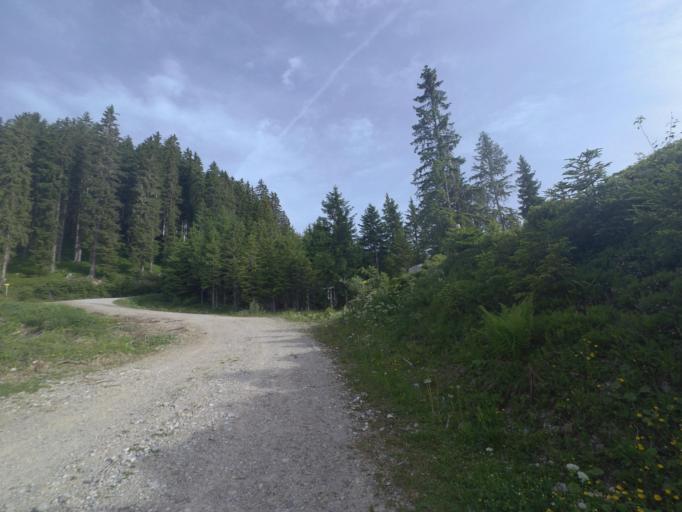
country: AT
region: Salzburg
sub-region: Politischer Bezirk Sankt Johann im Pongau
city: Muhlbach am Hochkonig
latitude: 47.3651
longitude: 13.1001
